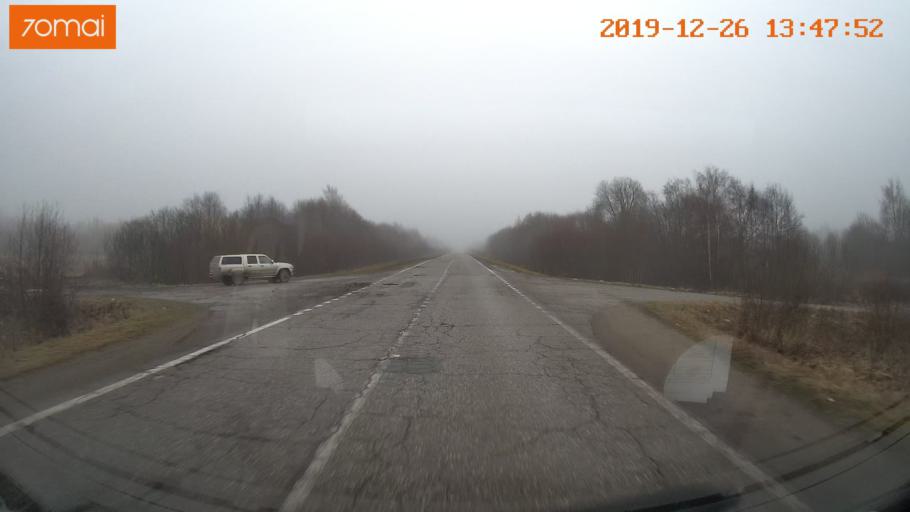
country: RU
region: Vologda
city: Sheksna
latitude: 58.6814
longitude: 38.5394
